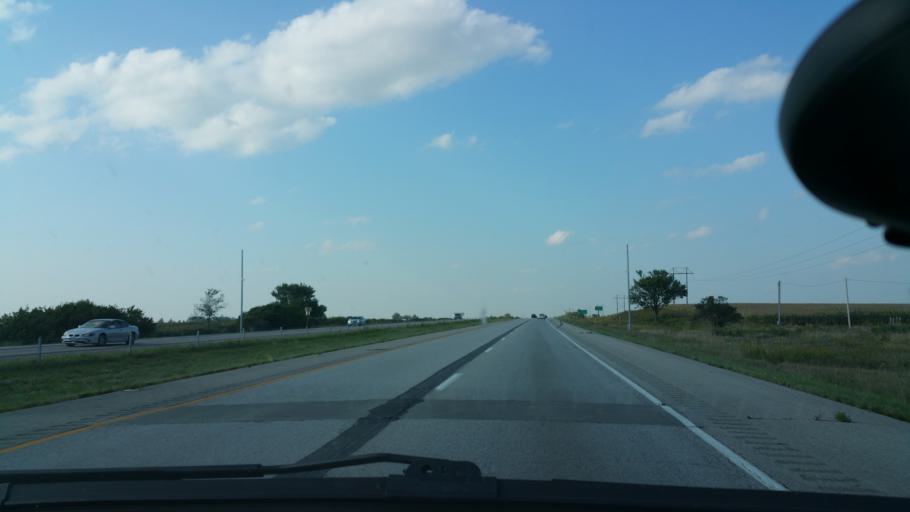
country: US
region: Iowa
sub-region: Story County
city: Huxley
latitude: 41.8622
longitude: -93.5711
